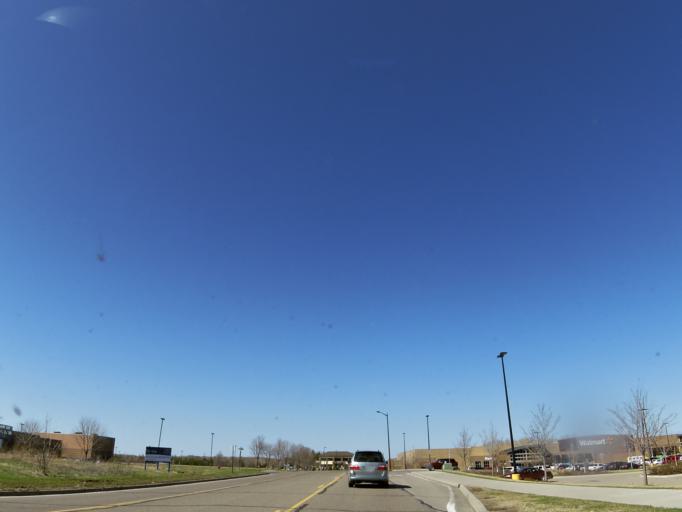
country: US
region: Minnesota
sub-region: Dakota County
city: Lakeville
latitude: 44.6484
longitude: -93.2983
